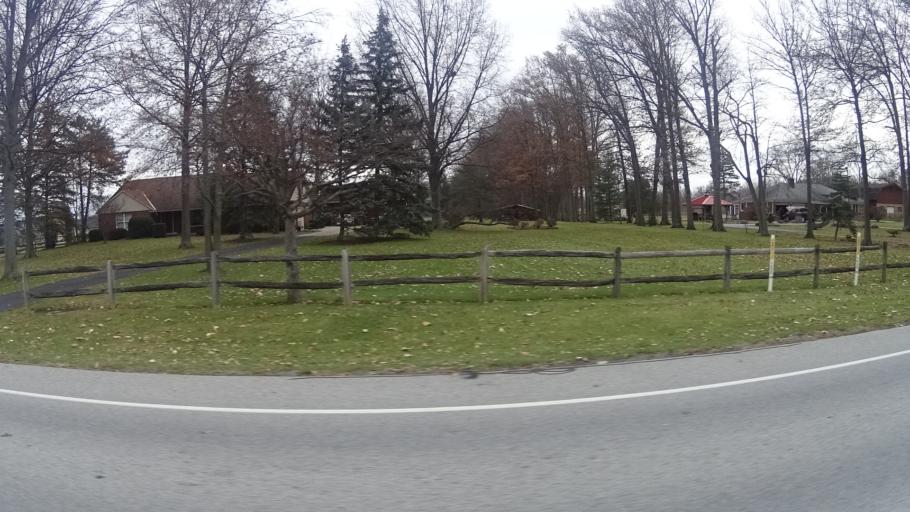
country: US
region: Ohio
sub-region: Cuyahoga County
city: Olmsted Falls
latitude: 41.3438
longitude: -81.9428
